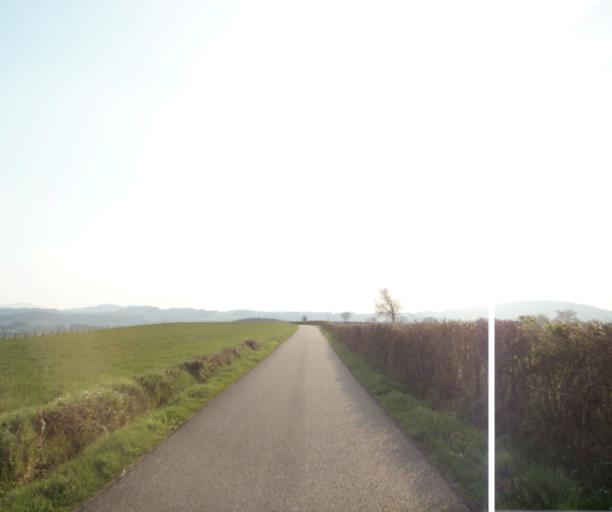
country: FR
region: Bourgogne
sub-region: Departement de Saone-et-Loire
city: Matour
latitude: 46.4145
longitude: 4.4563
